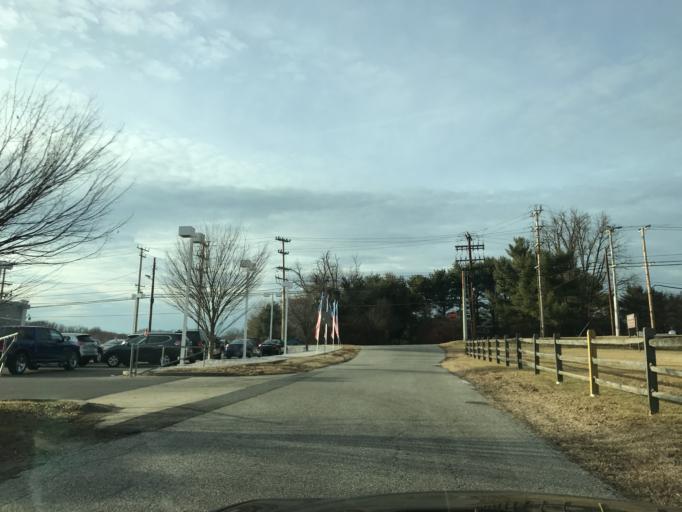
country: US
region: Maryland
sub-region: Baltimore County
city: Kingsville
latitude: 39.4453
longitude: -76.4200
